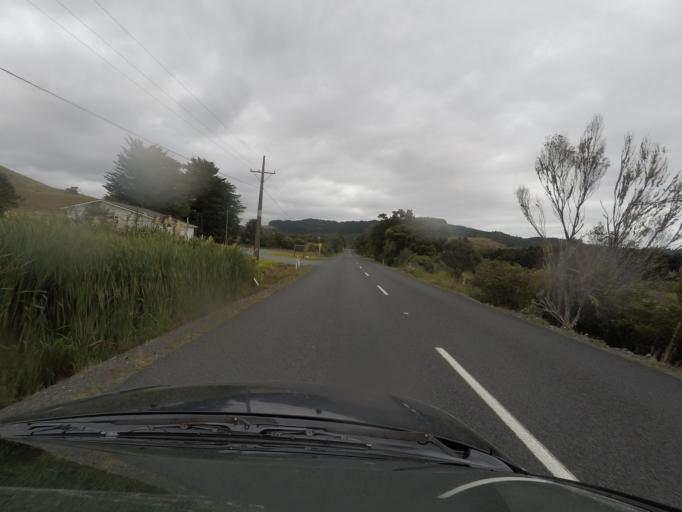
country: NZ
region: Auckland
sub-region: Auckland
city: Warkworth
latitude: -36.2843
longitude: 174.6451
